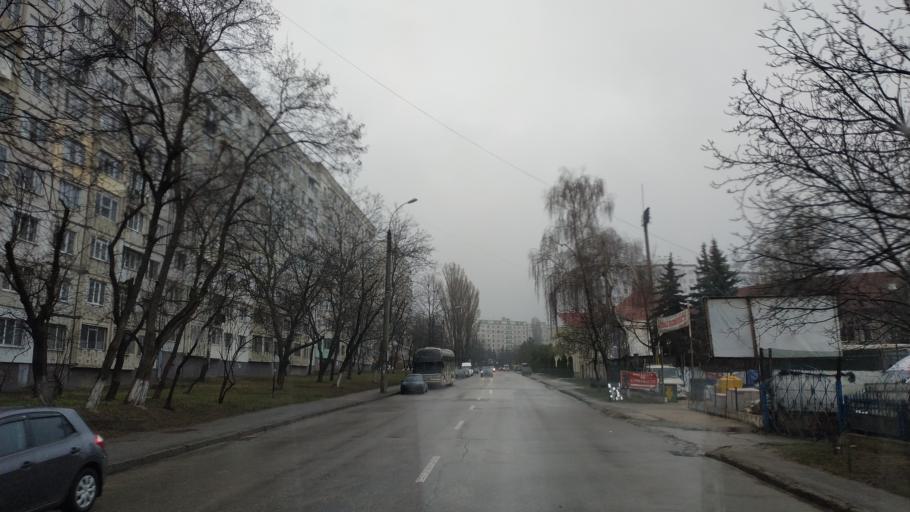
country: MD
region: Chisinau
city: Vatra
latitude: 47.0415
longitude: 28.7740
